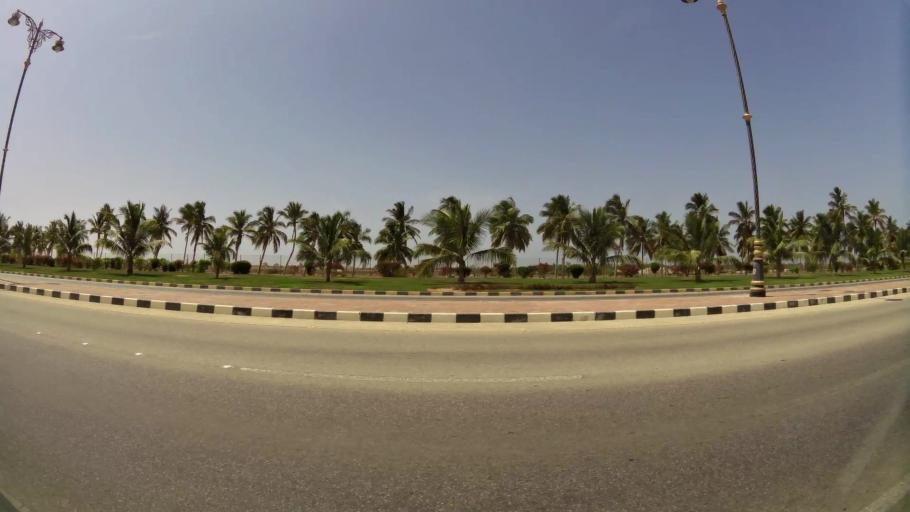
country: OM
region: Zufar
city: Salalah
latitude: 17.0487
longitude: 54.2139
